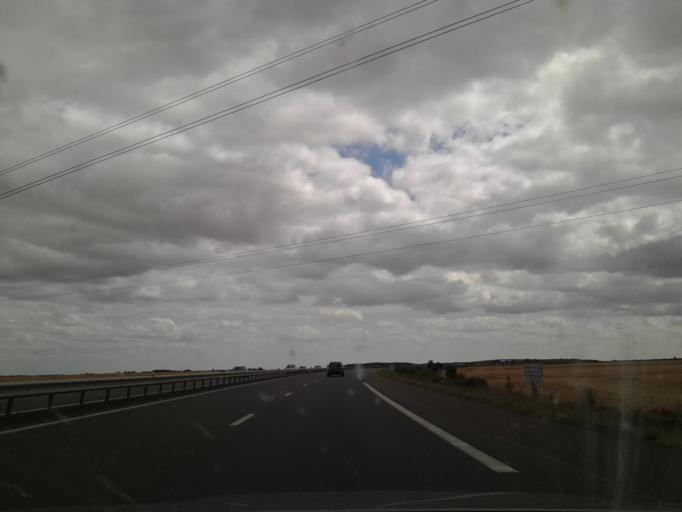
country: FR
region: Centre
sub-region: Departement du Cher
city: Plaimpied-Givaudins
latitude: 46.9710
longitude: 2.4249
